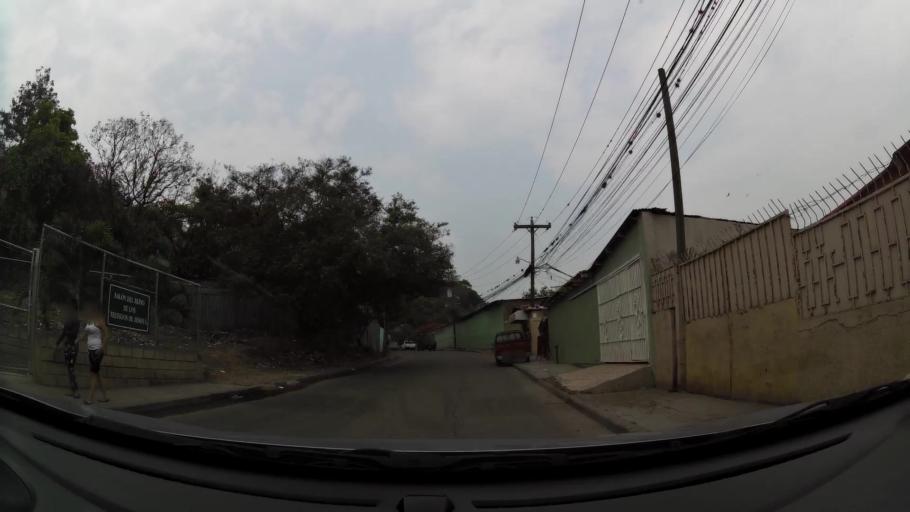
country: HN
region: Francisco Morazan
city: Tegucigalpa
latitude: 14.0767
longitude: -87.2277
